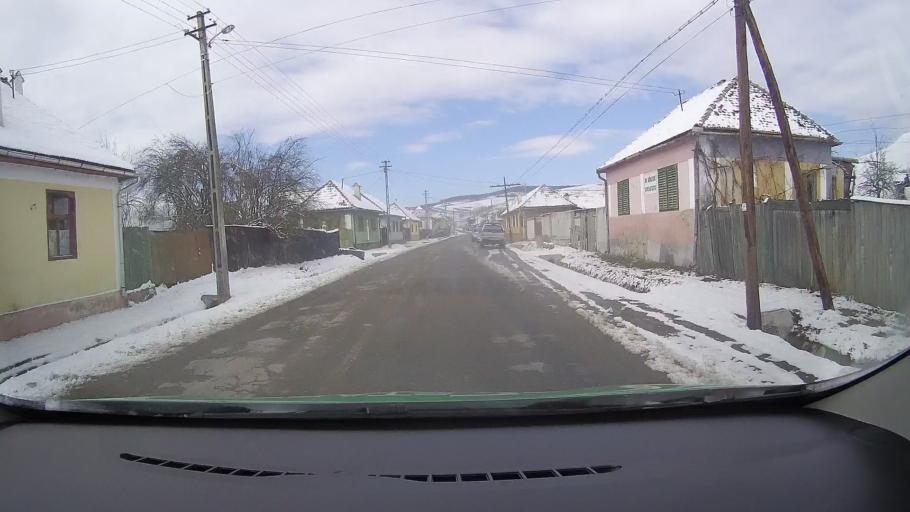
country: RO
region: Sibiu
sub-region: Comuna Altina
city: Altina
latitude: 45.9846
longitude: 24.4543
